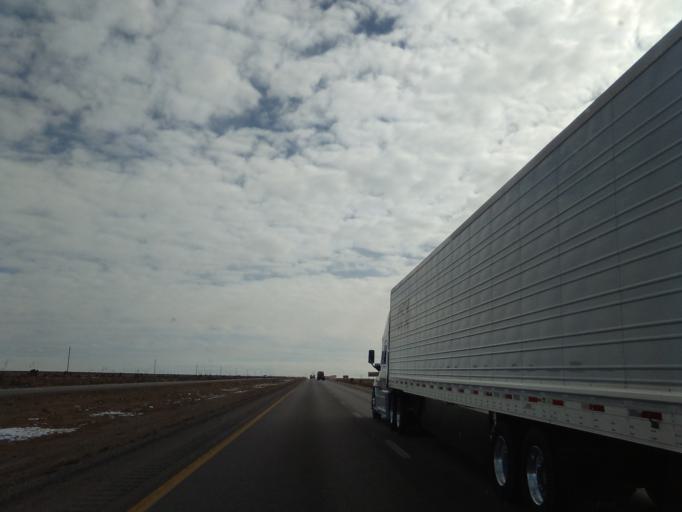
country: US
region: New Mexico
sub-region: Hidalgo County
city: Lordsburg
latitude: 32.2505
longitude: -108.5037
